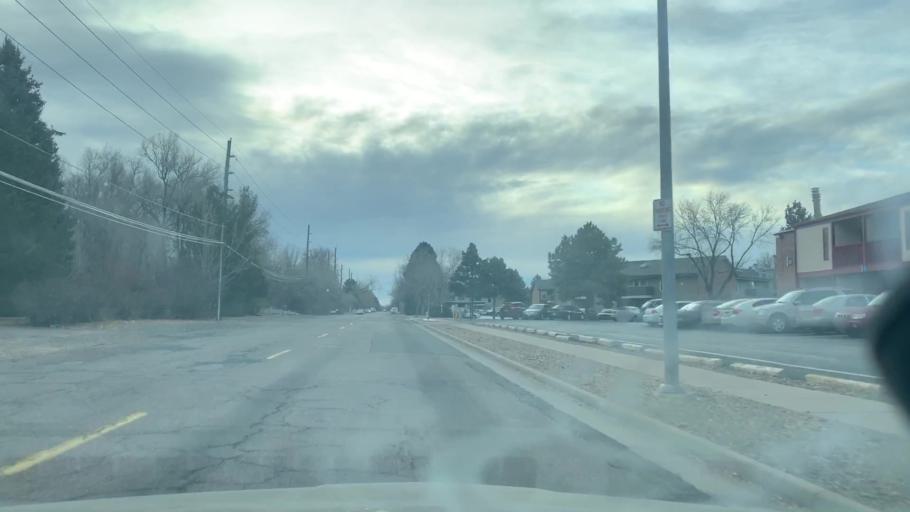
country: US
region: Colorado
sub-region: Arapahoe County
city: Glendale
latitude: 39.6936
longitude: -104.9007
